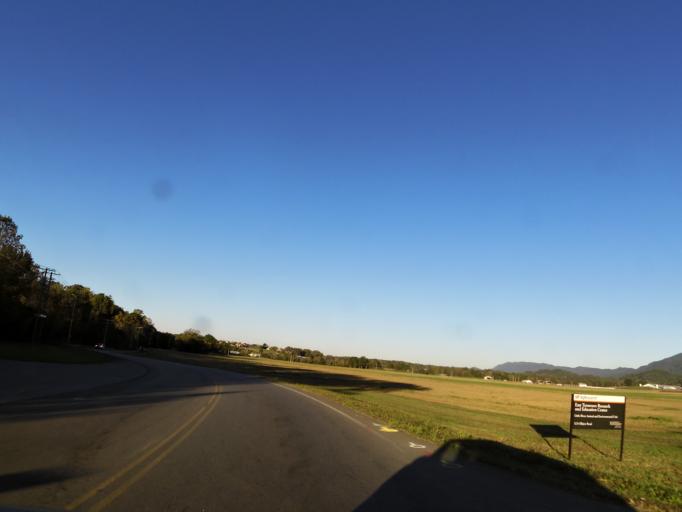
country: US
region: Tennessee
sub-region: Blount County
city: Wildwood
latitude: 35.7660
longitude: -83.8560
